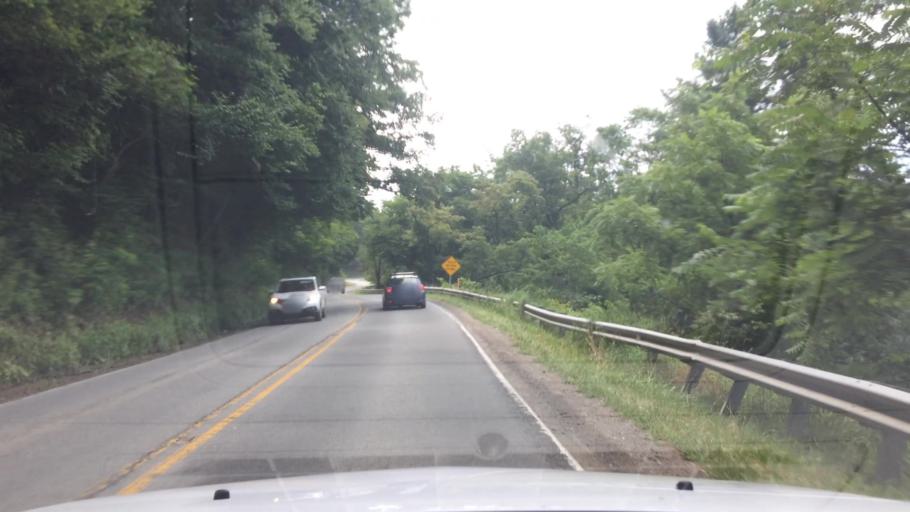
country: US
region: North Carolina
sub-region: Watauga County
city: Boone
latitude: 36.2186
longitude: -81.6379
